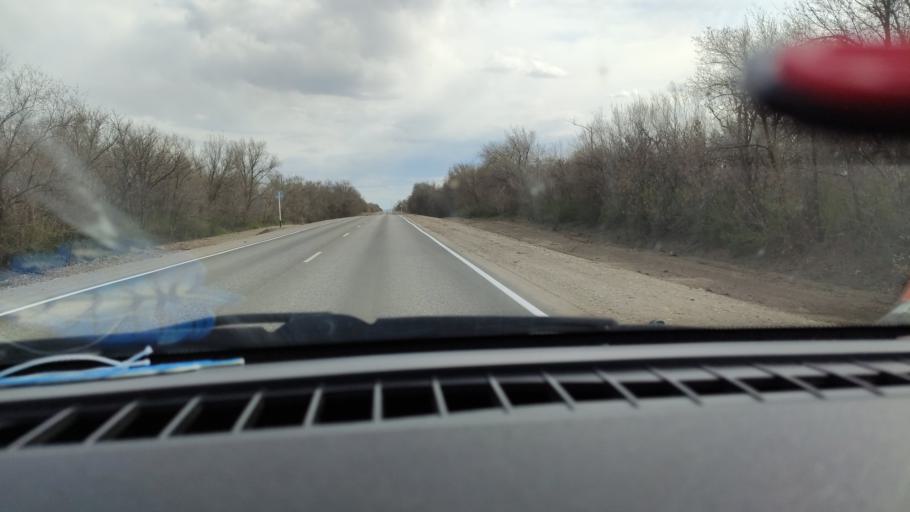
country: RU
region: Saratov
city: Krasnoarmeysk
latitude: 51.0941
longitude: 45.9558
